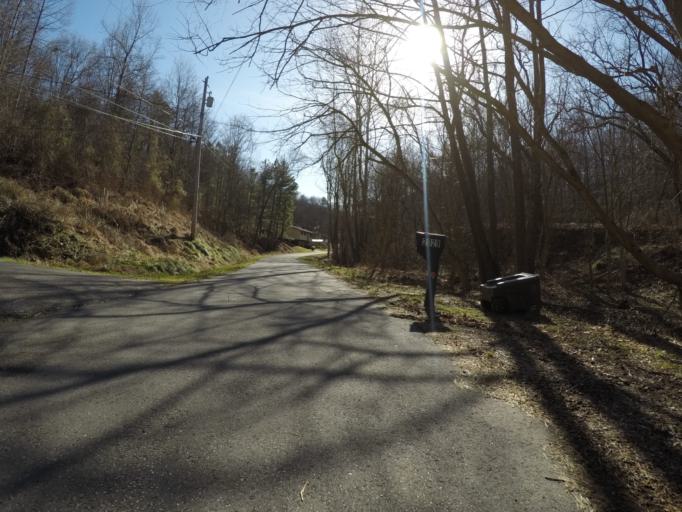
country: US
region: Kentucky
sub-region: Boyd County
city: Catlettsburg
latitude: 38.4165
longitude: -82.6086
